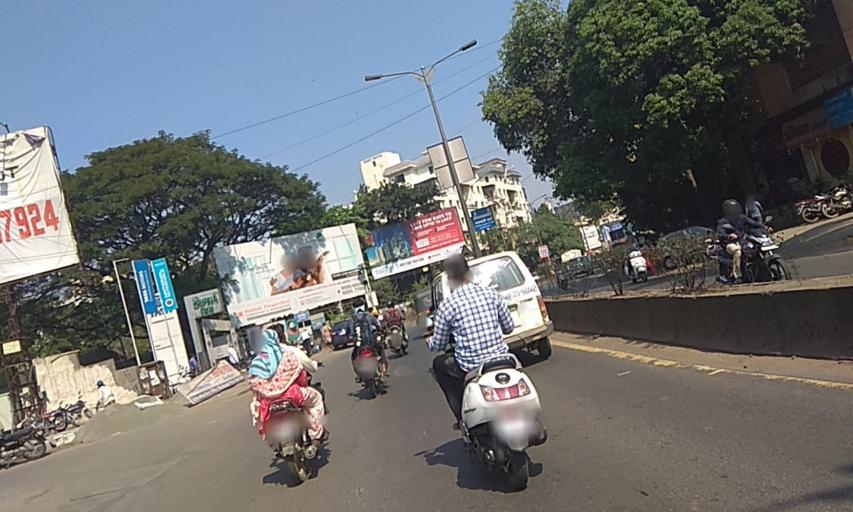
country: IN
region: Maharashtra
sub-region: Pune Division
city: Pune
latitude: 18.5059
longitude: 73.9277
